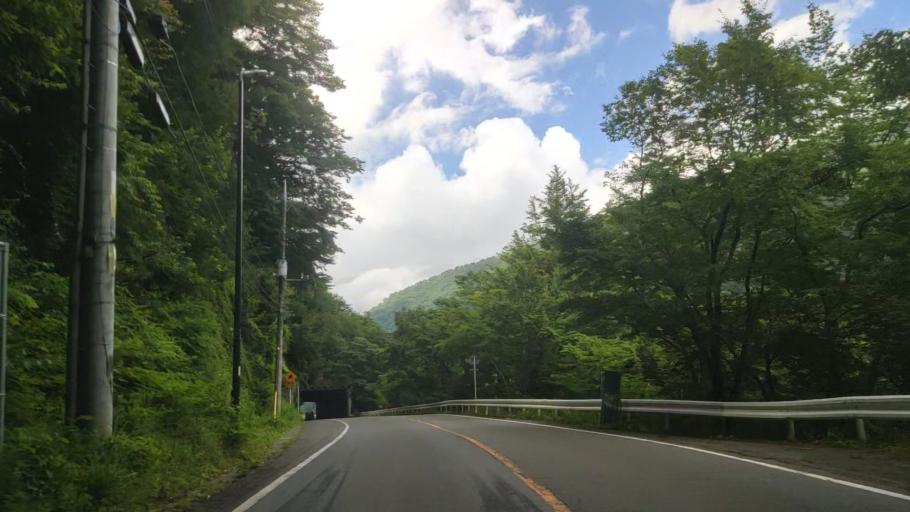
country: JP
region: Yamanashi
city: Enzan
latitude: 35.9148
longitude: 138.8302
